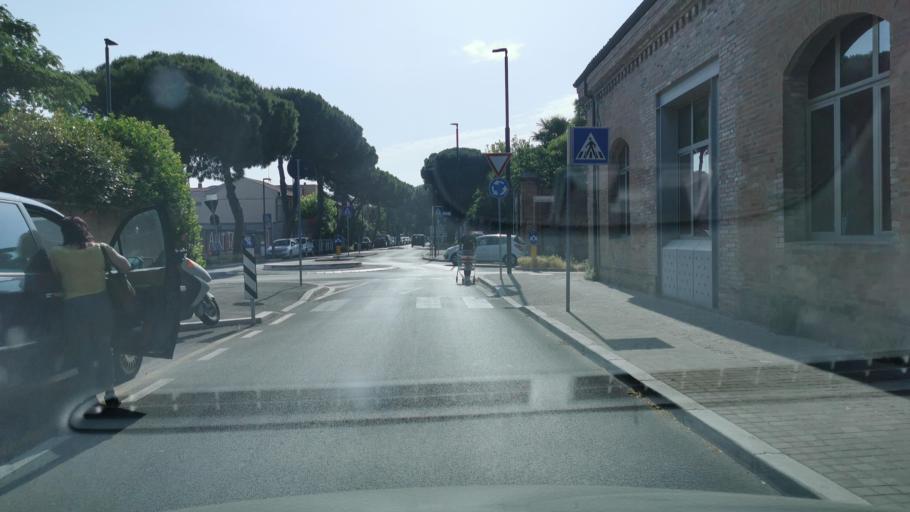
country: IT
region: Emilia-Romagna
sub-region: Provincia di Ravenna
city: Ravenna
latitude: 44.4116
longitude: 12.2036
